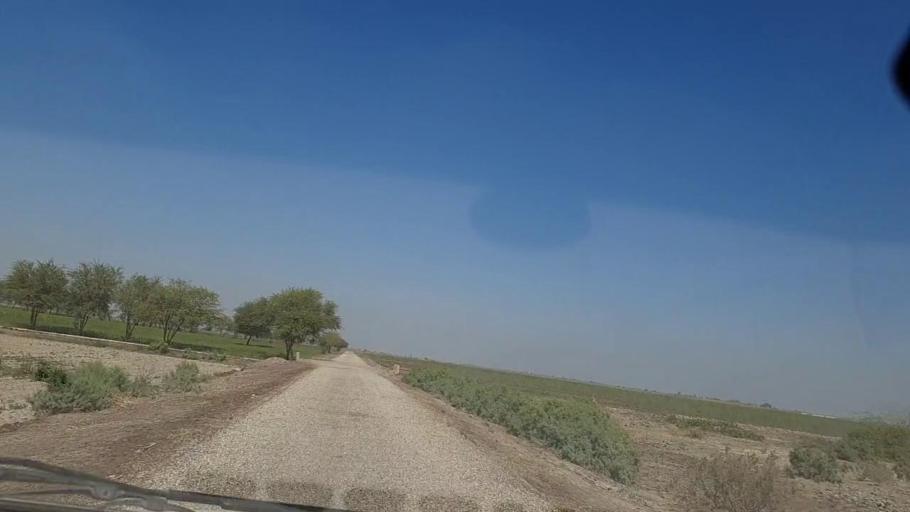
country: PK
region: Sindh
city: Mirpur Khas
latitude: 25.4352
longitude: 69.0510
